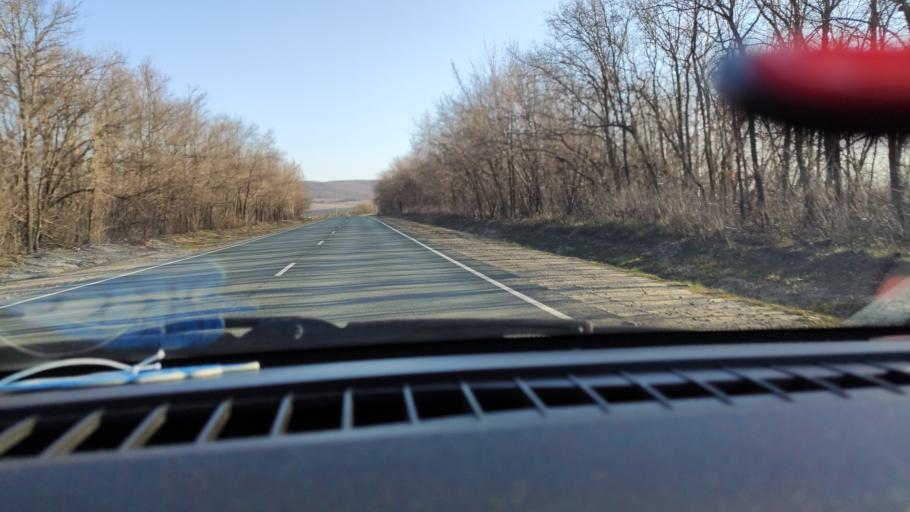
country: RU
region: Saratov
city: Alekseyevka
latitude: 52.2738
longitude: 47.9303
